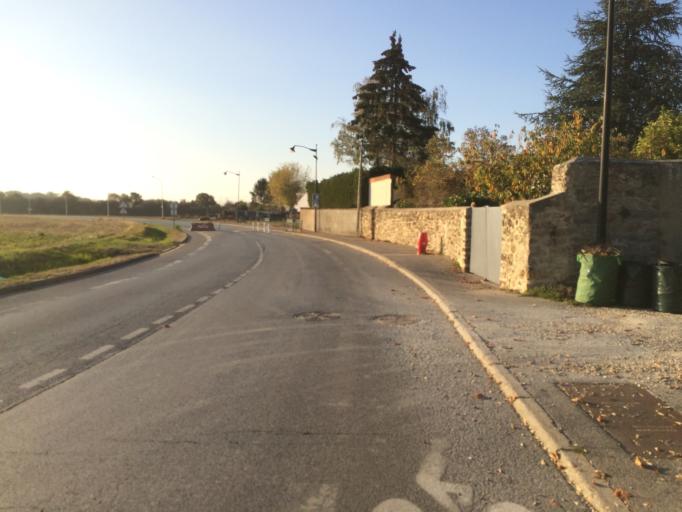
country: FR
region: Ile-de-France
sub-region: Departement de l'Essonne
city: Nozay
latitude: 48.6616
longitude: 2.2298
